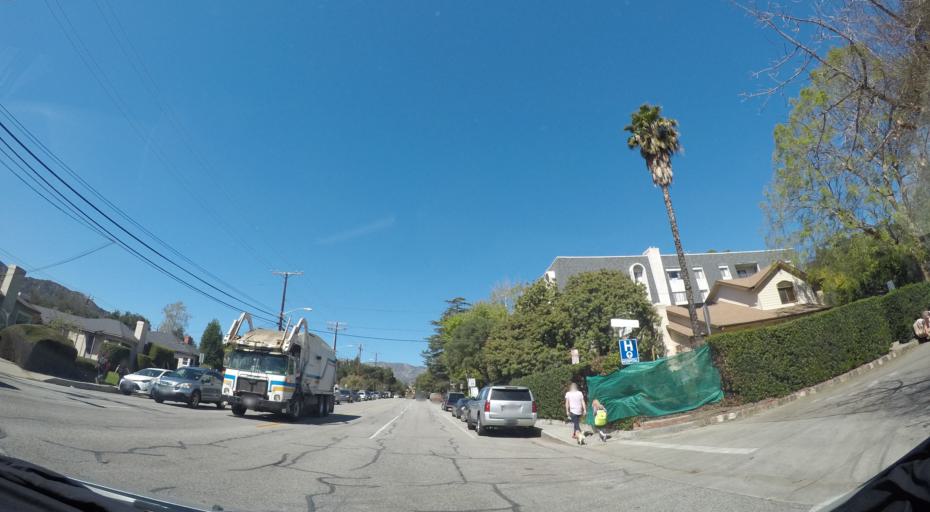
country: US
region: California
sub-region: Los Angeles County
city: North Glendale
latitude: 34.1749
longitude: -118.2260
